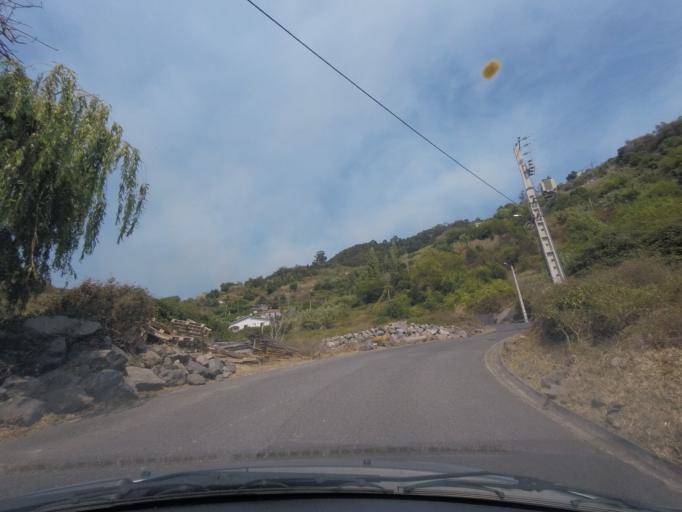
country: PT
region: Madeira
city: Ribeira Brava
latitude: 32.6897
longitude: -17.0676
